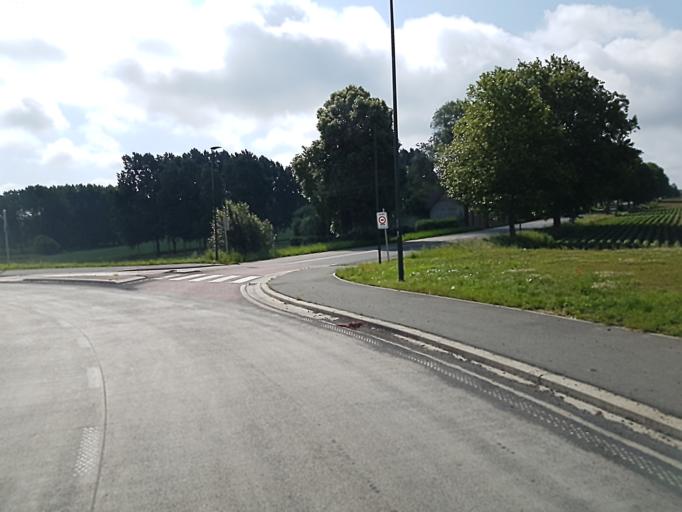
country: BE
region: Wallonia
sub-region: Province du Hainaut
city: Soignies
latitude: 50.5935
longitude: 4.0616
